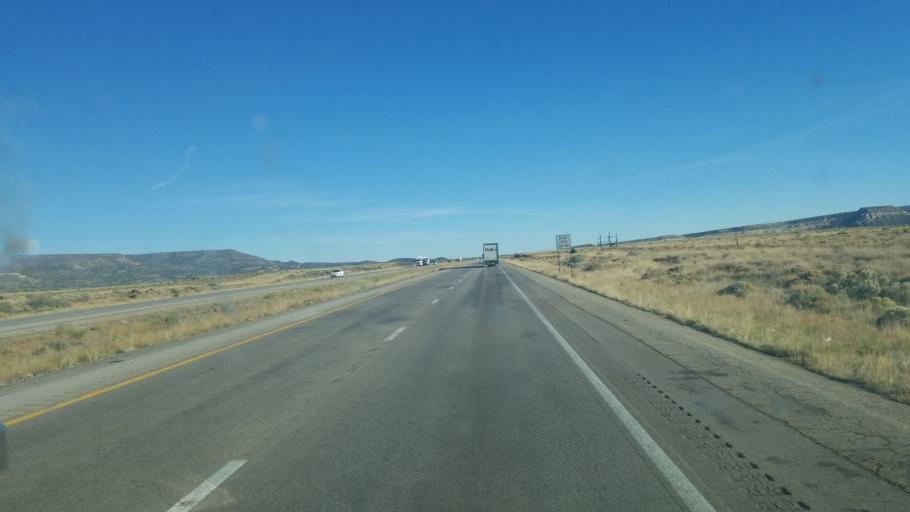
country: US
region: New Mexico
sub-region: Cibola County
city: Grants
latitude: 35.1123
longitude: -107.8121
